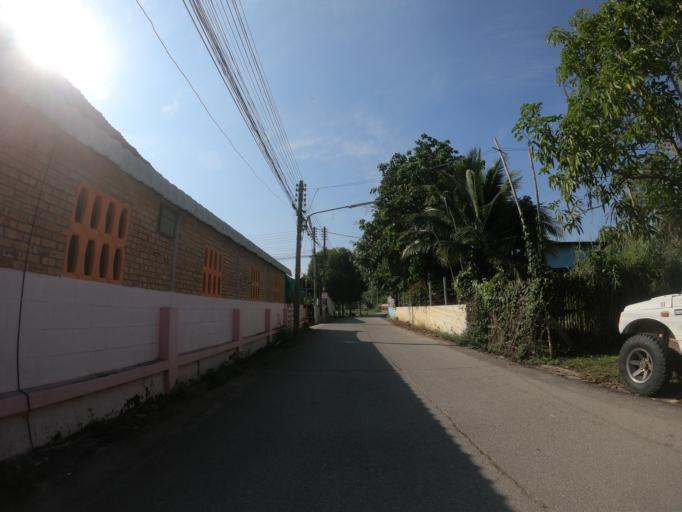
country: TH
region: Chiang Mai
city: Chiang Mai
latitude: 18.7422
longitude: 98.9866
